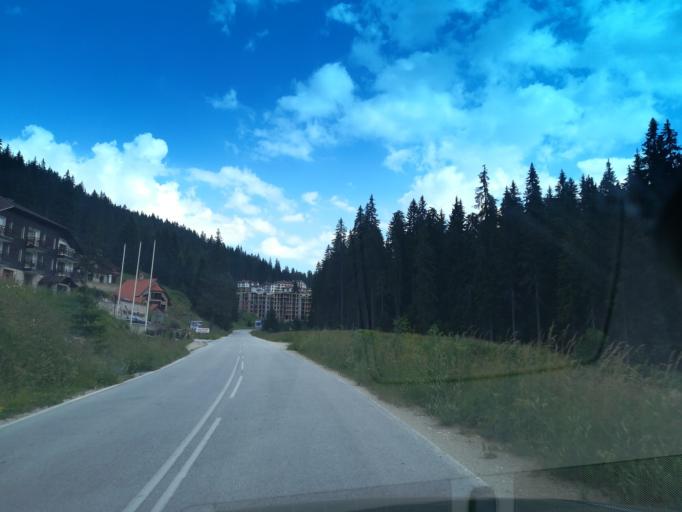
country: BG
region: Smolyan
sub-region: Obshtina Smolyan
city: Smolyan
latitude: 41.6568
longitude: 24.6848
